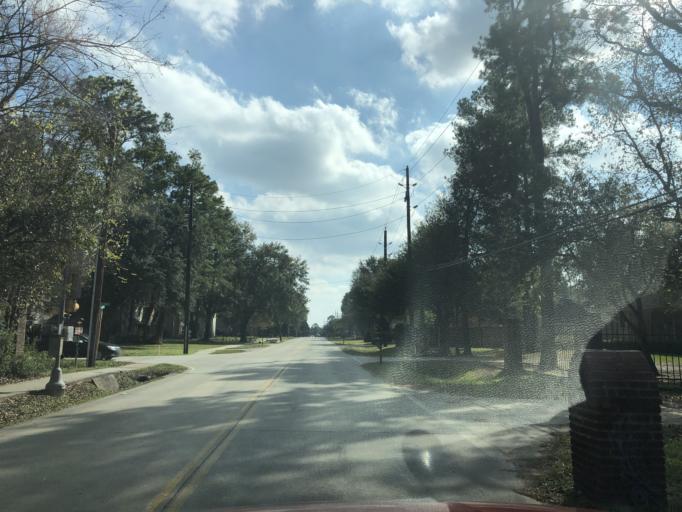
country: US
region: Texas
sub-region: Harris County
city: Tomball
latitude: 30.0287
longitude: -95.5438
